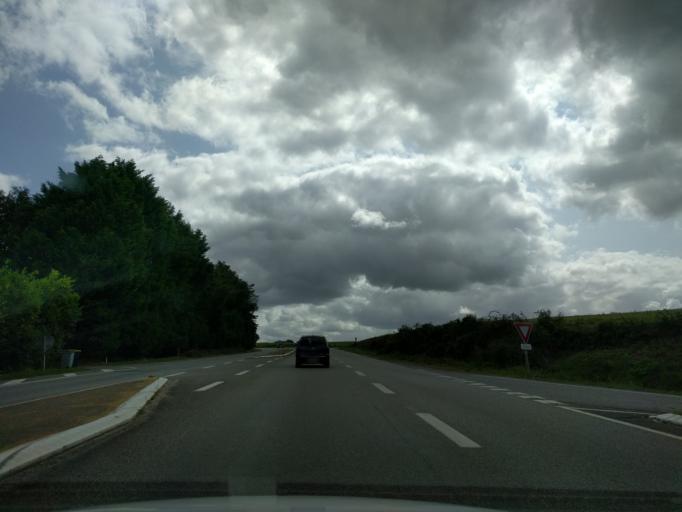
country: FR
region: Brittany
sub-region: Departement du Morbihan
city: Caudan
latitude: 47.8293
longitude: -3.3381
